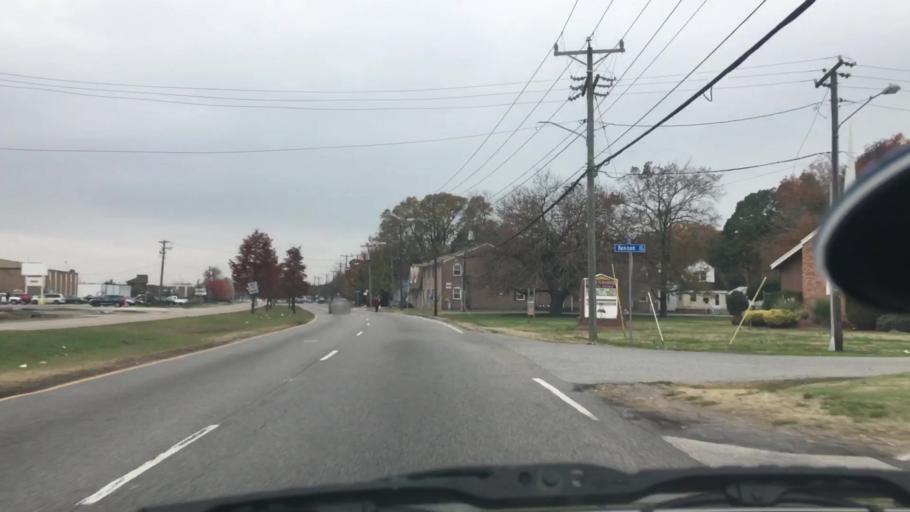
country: US
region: Virginia
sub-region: City of Norfolk
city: Norfolk
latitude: 36.8664
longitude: -76.2368
